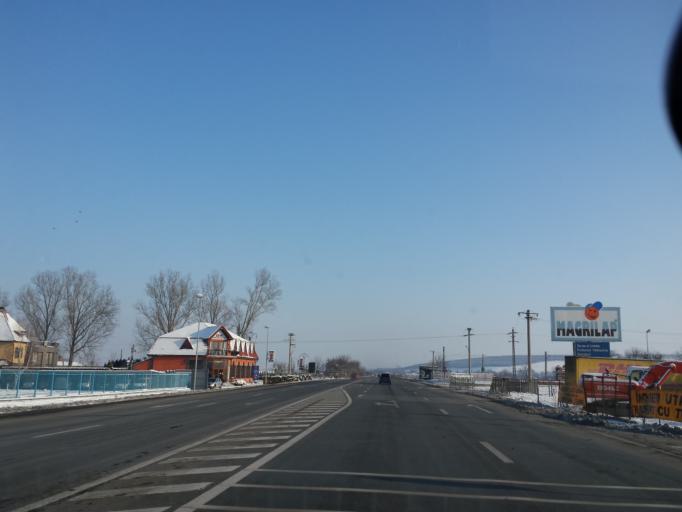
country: RO
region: Hunedoara
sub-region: Municipiul Deva
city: Cristur
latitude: 45.8540
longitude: 22.9631
